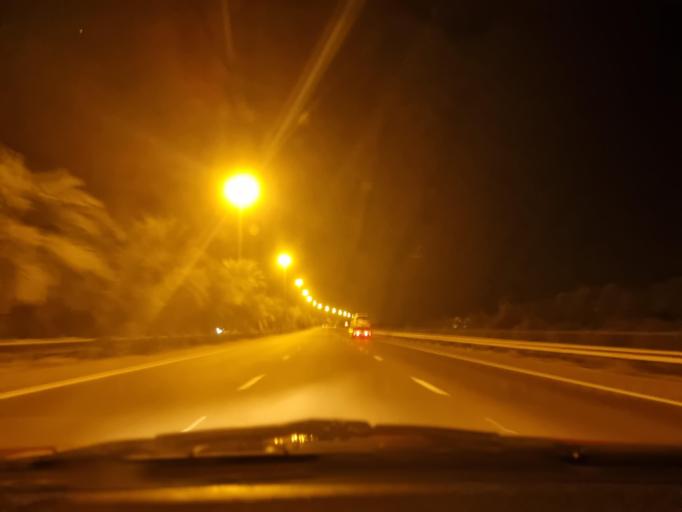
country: AE
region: Abu Dhabi
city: Al Ain
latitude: 24.1795
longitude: 55.1584
